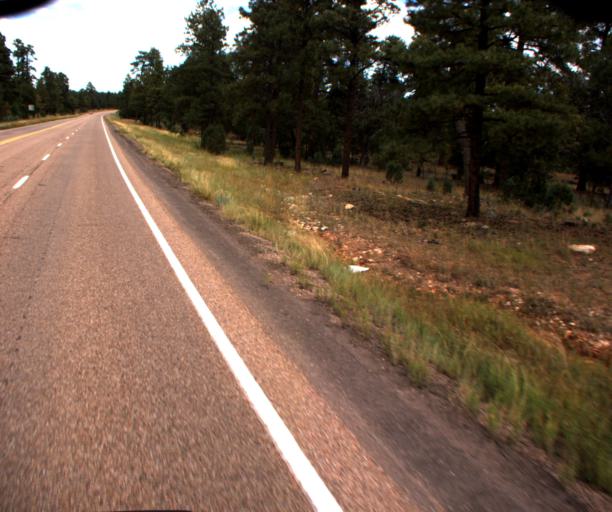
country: US
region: Arizona
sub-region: Navajo County
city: Heber-Overgaard
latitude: 34.3974
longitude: -110.6707
